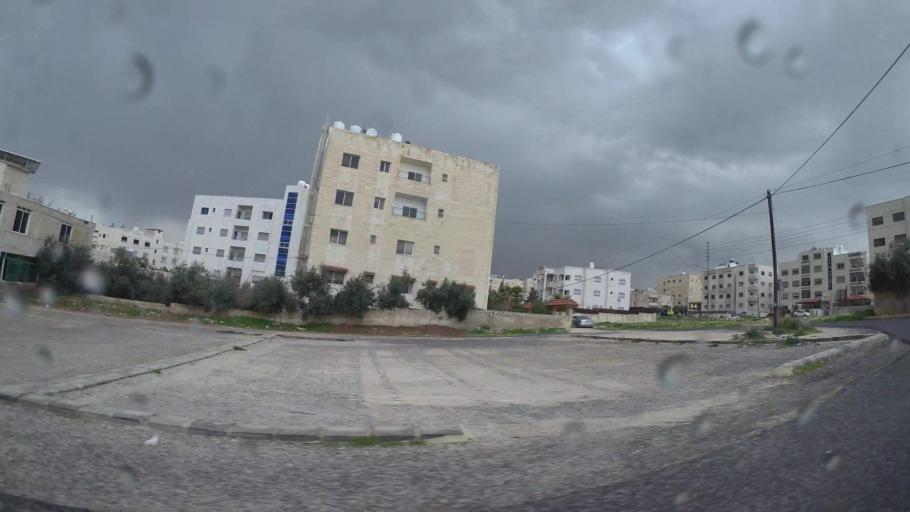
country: JO
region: Amman
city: Amman
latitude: 32.0079
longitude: 35.9582
